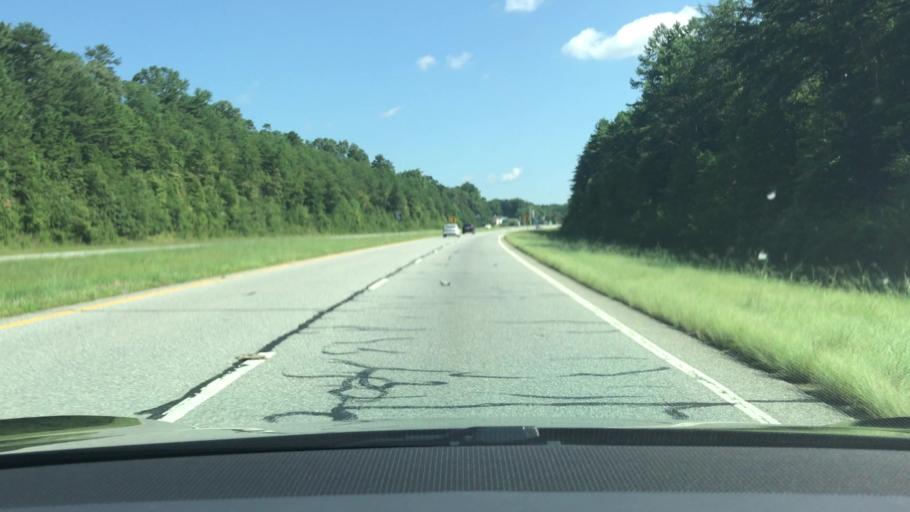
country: US
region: Georgia
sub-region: Habersham County
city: Clarkesville
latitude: 34.6417
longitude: -83.4507
